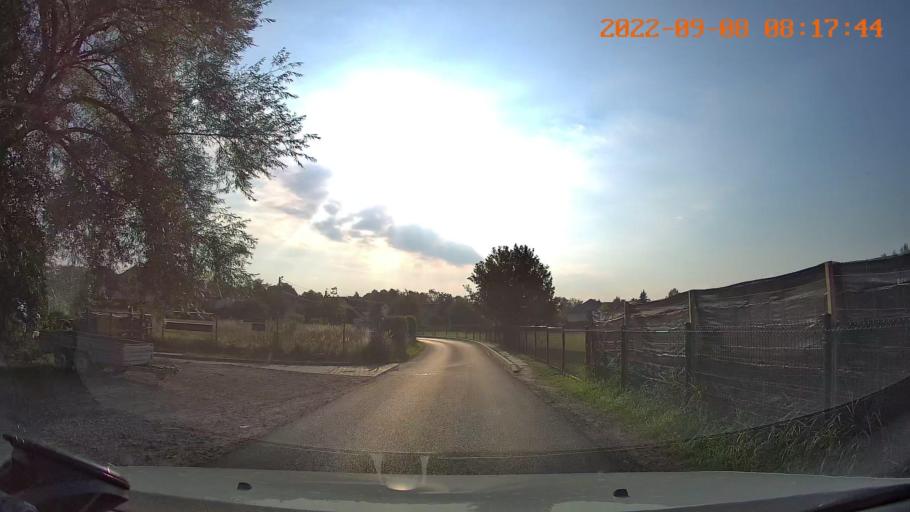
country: PL
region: Lesser Poland Voivodeship
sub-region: Powiat krakowski
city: Rzaska
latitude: 50.0710
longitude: 19.8826
